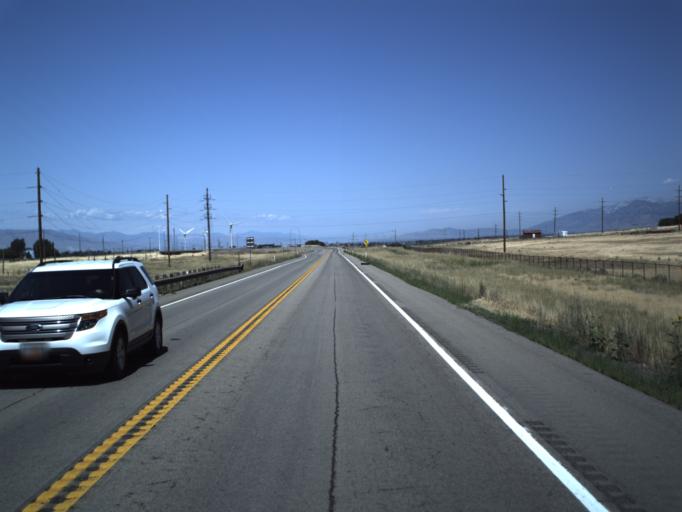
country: US
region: Utah
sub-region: Utah County
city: Mapleton
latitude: 40.0776
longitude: -111.5826
